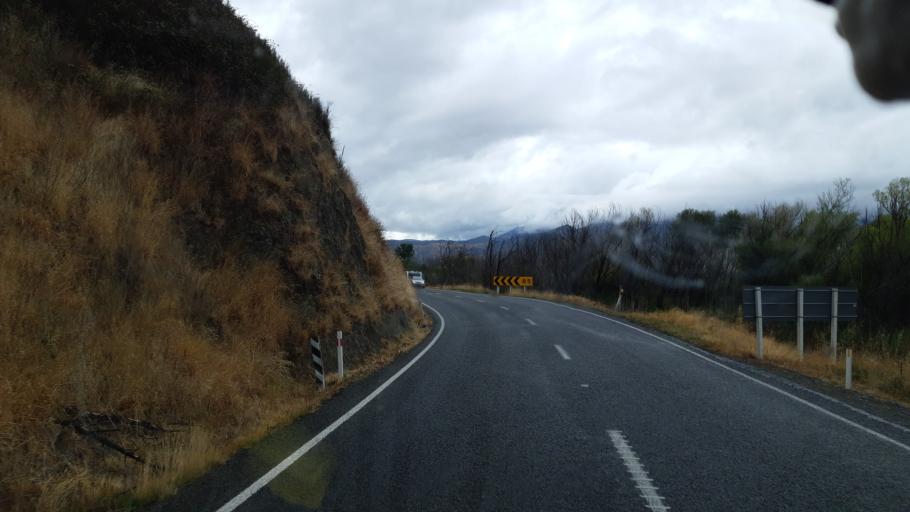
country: NZ
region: Canterbury
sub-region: Hurunui District
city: Amberley
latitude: -42.5780
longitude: 172.7423
